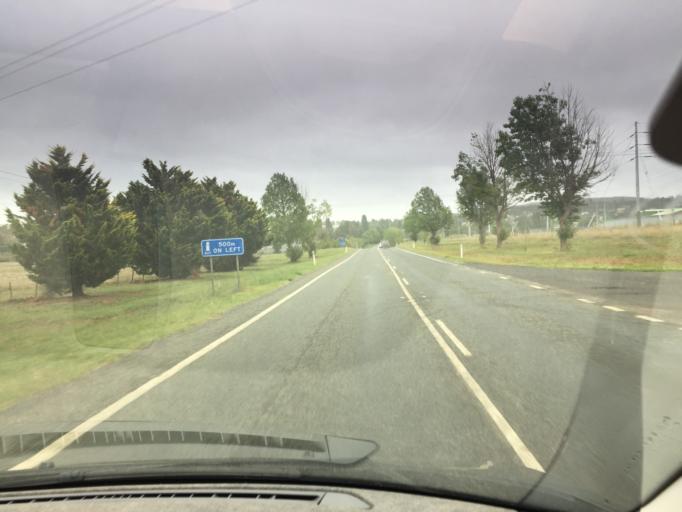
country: AU
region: New South Wales
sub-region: Cooma-Monaro
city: Cooma
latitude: -36.2157
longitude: 149.1448
